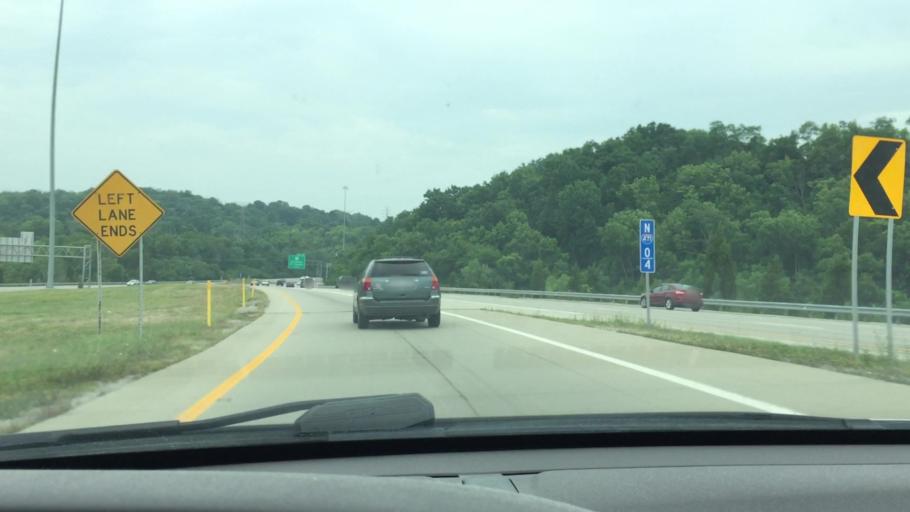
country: US
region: Kentucky
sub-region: Campbell County
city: Highland Heights
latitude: 39.0502
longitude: -84.4642
